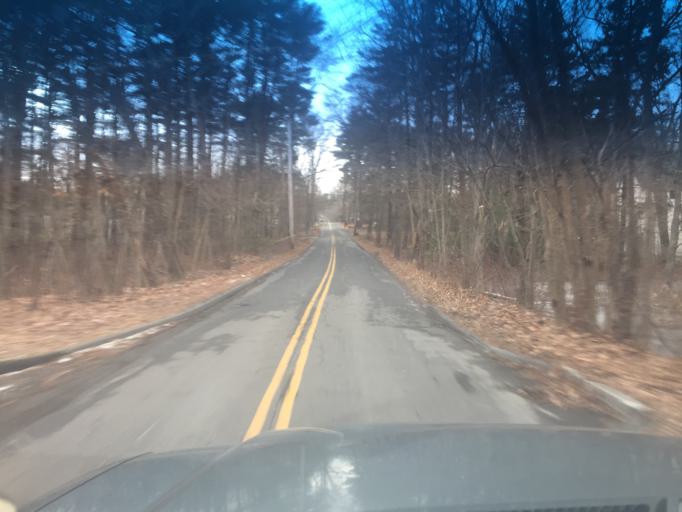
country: US
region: Massachusetts
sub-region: Norfolk County
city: Bellingham
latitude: 42.1167
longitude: -71.4464
